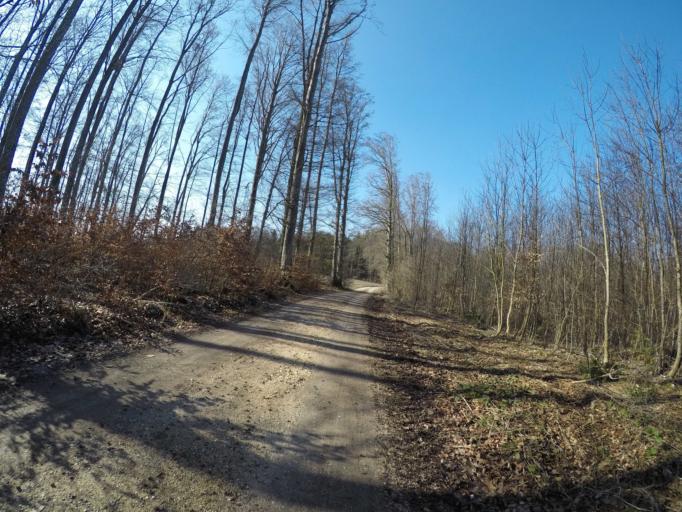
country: DE
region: Baden-Wuerttemberg
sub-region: Tuebingen Region
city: Blaubeuren
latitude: 48.3797
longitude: 9.8315
